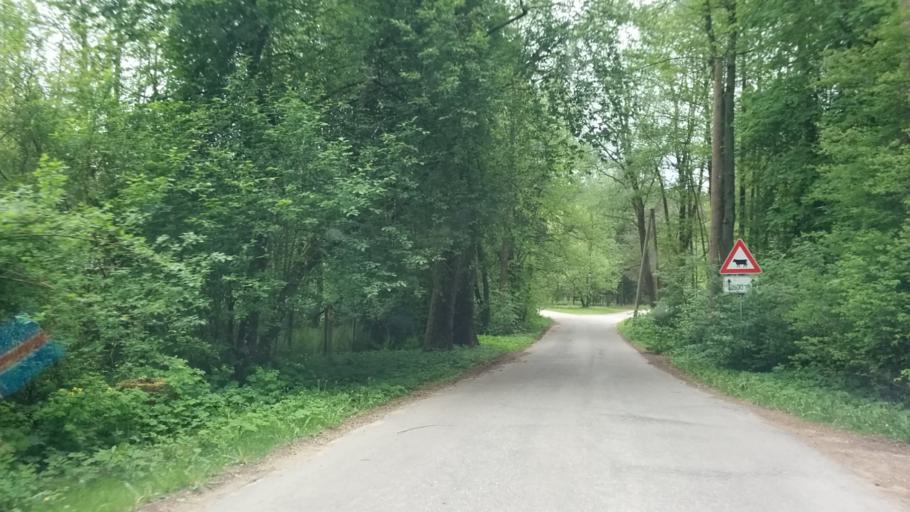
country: LV
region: Babite
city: Pinki
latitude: 56.9340
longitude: 23.9338
